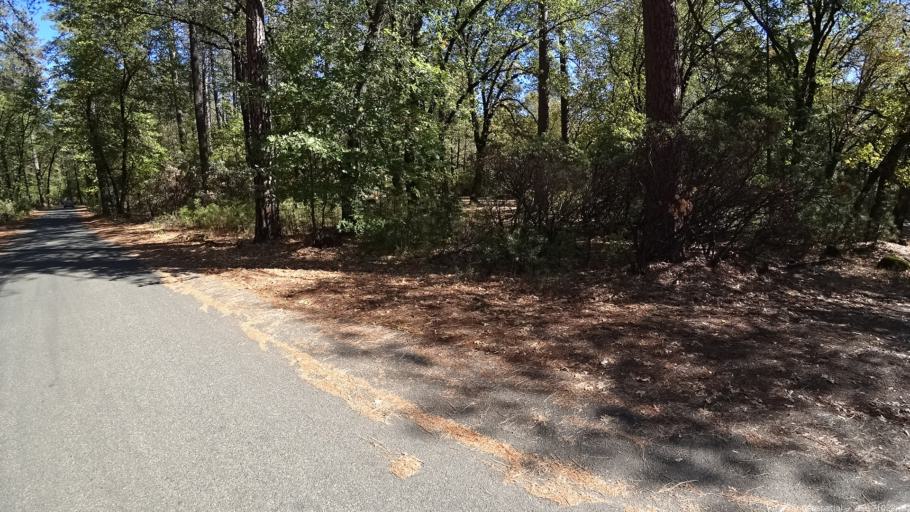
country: US
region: California
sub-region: Shasta County
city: Central Valley (historical)
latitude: 40.8873
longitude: -122.3797
